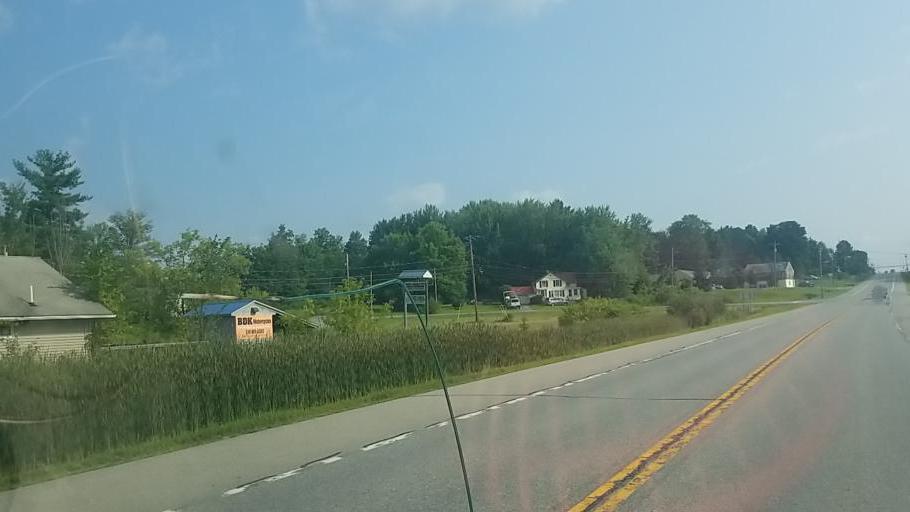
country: US
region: New York
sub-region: Fulton County
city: Gloversville
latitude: 43.1032
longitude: -74.2739
